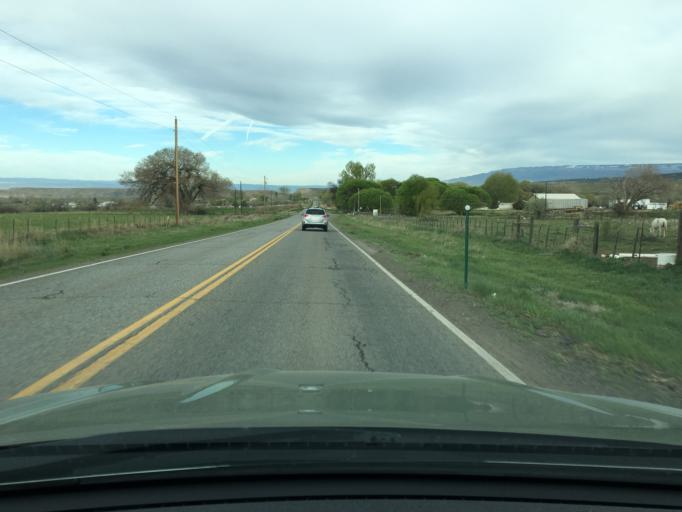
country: US
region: Colorado
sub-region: Delta County
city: Cedaredge
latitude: 38.8004
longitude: -107.7986
